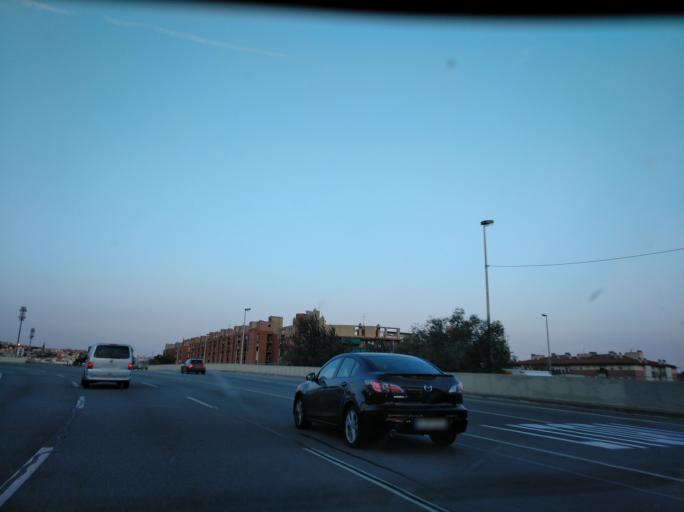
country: ES
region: Catalonia
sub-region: Provincia de Barcelona
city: Santa Coloma de Gramenet
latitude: 41.4477
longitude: 2.1964
